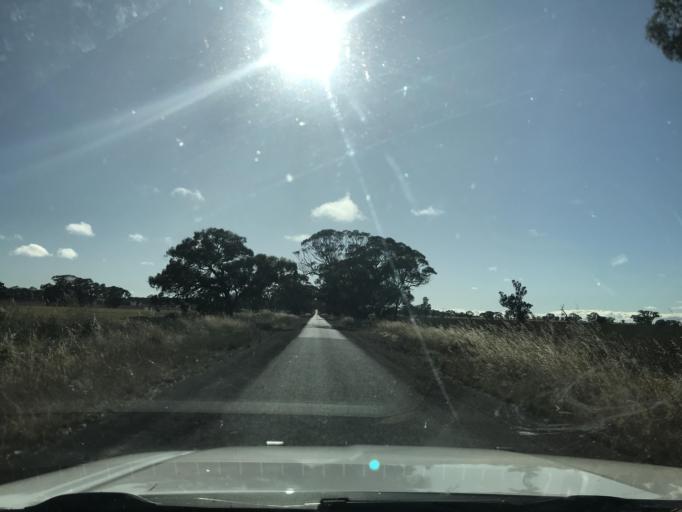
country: AU
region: Victoria
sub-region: Horsham
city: Horsham
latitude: -36.6983
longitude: 141.6074
